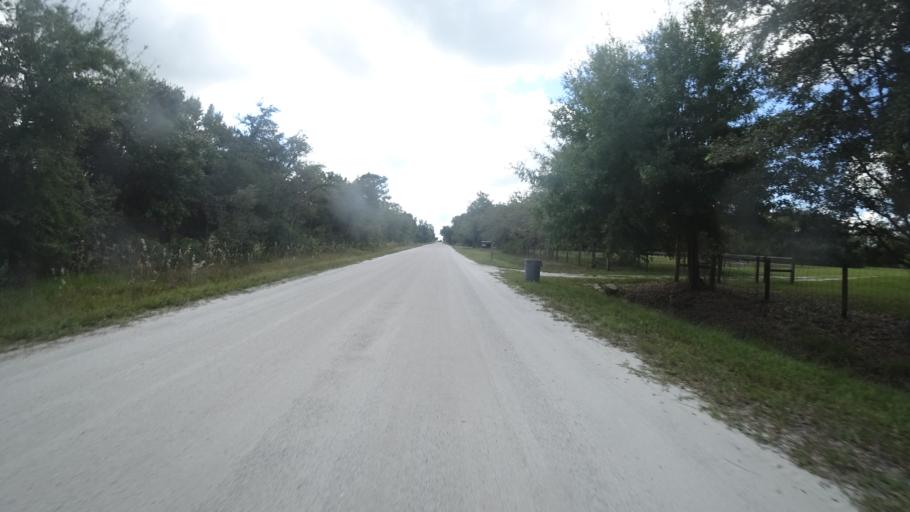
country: US
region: Florida
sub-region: Sarasota County
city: Lake Sarasota
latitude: 27.3766
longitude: -82.2194
